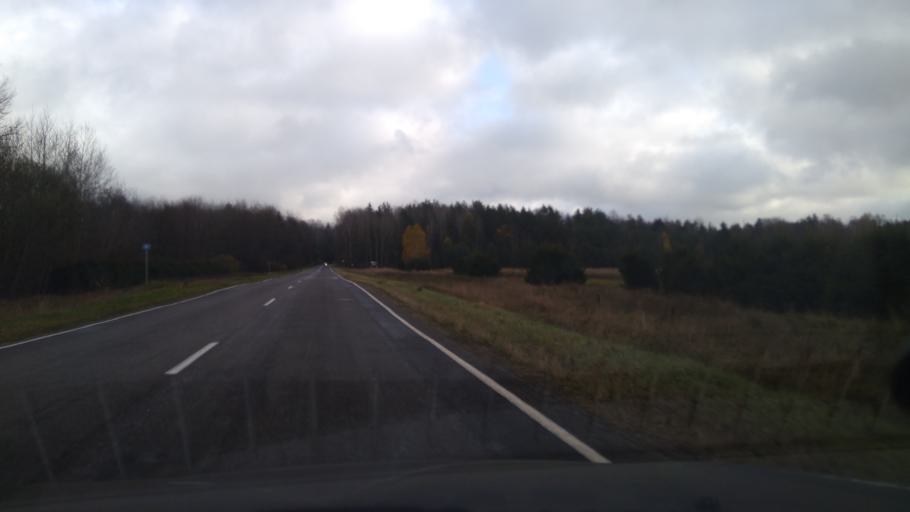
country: BY
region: Minsk
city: Slutsk
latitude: 53.2311
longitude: 27.6320
